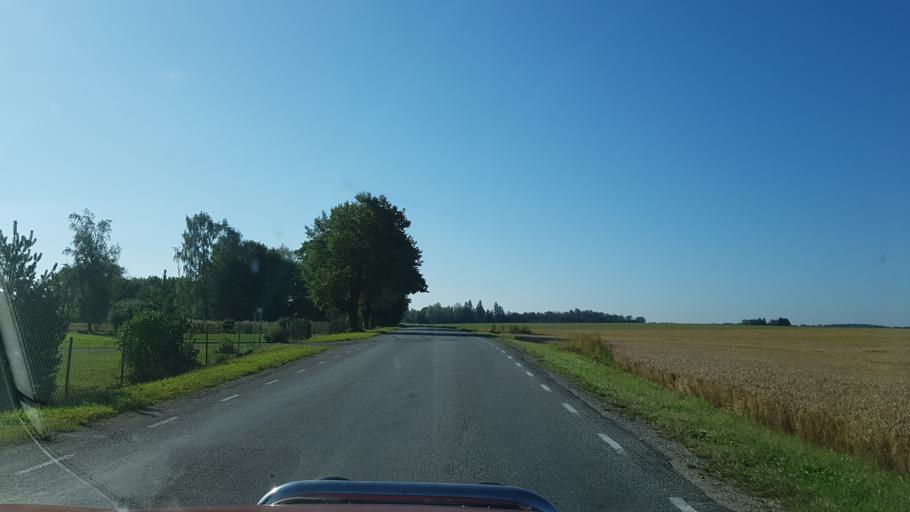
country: EE
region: Jogevamaa
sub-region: Jogeva linn
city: Jogeva
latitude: 58.7133
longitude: 26.4036
